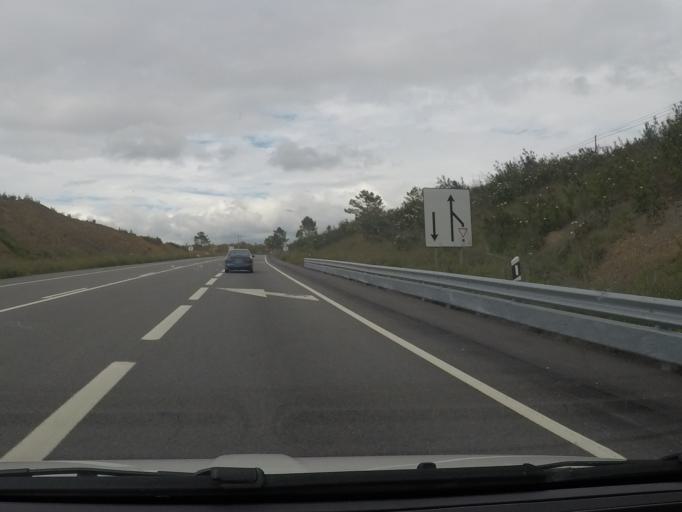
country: PT
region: Setubal
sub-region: Santiago do Cacem
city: Santiago do Cacem
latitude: 38.0658
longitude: -8.6971
